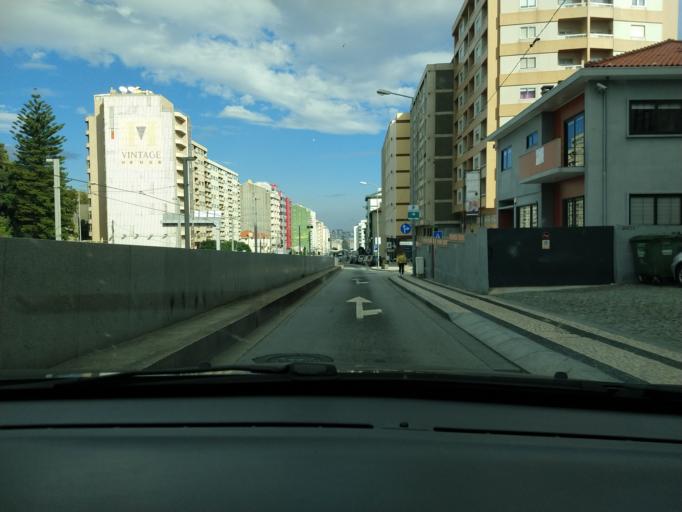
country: PT
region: Porto
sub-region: Vila Nova de Gaia
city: Vilar de Andorinho
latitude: 41.1164
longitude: -8.6063
